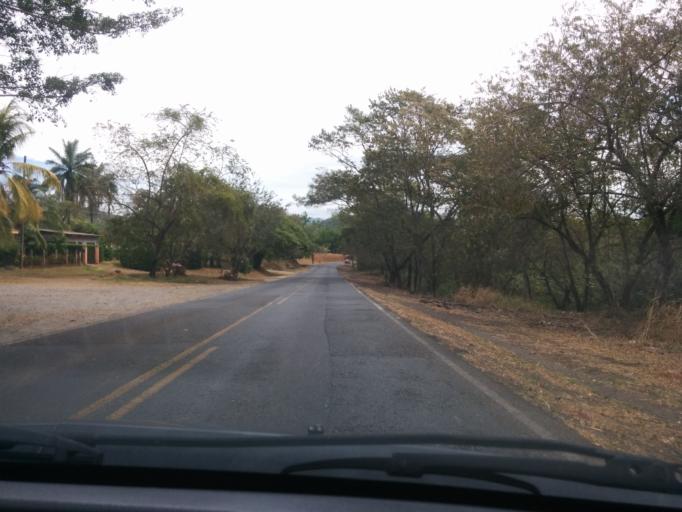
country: CR
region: Puntarenas
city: Esparza
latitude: 10.0047
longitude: -84.6316
